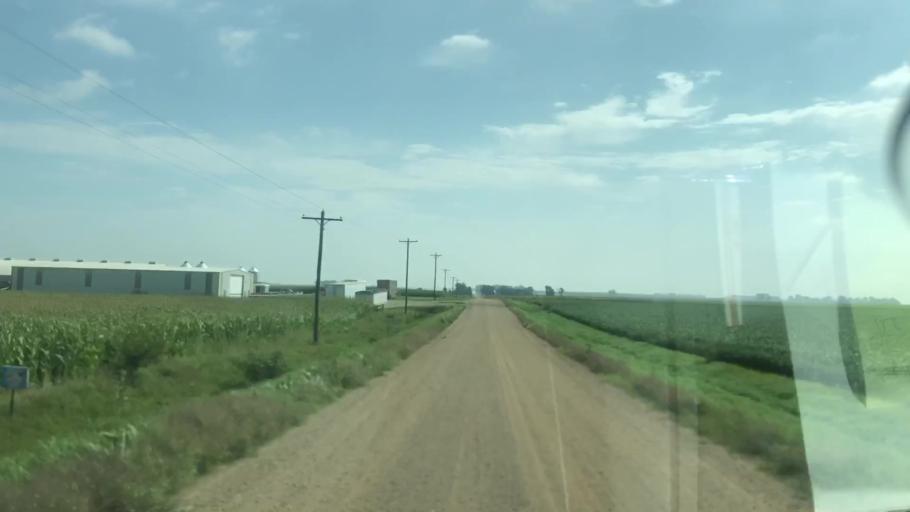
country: US
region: Iowa
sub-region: O'Brien County
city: Sheldon
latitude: 43.2153
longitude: -95.9754
